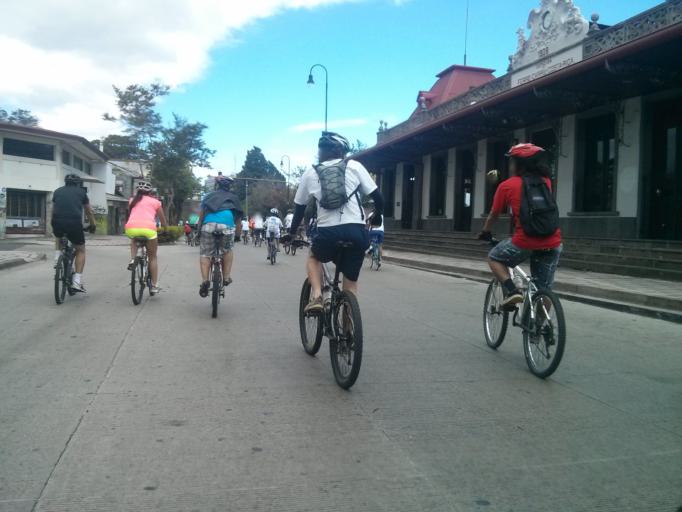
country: CR
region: San Jose
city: San Jose
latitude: 9.9345
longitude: -84.0687
